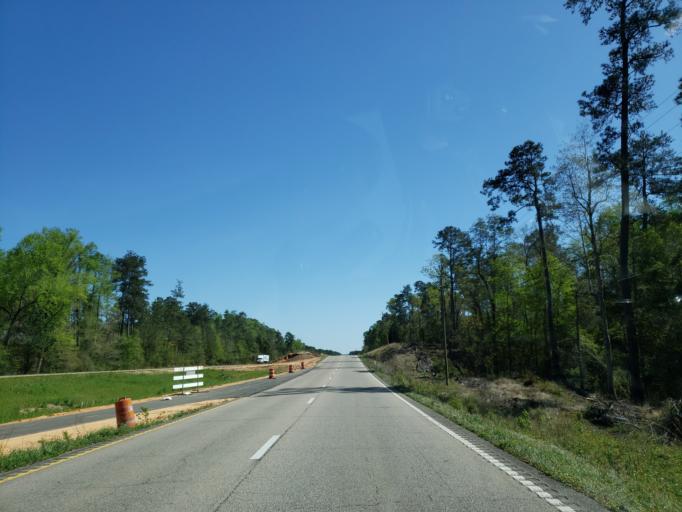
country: US
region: Mississippi
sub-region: Lamar County
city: Purvis
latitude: 31.1448
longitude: -89.2340
